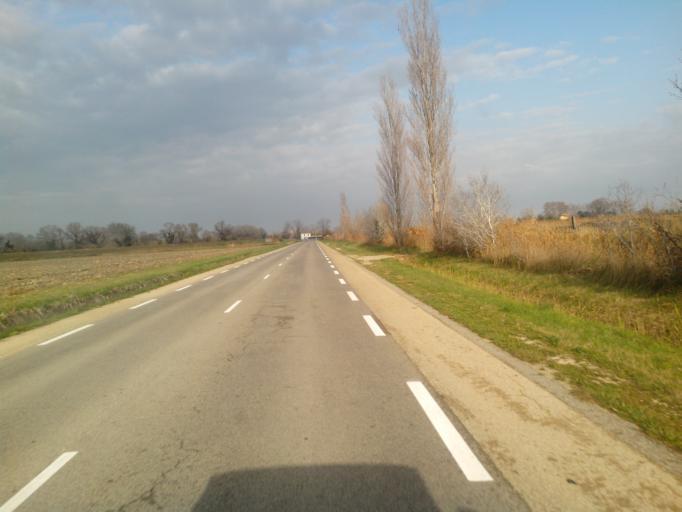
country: FR
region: Languedoc-Roussillon
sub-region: Departement du Gard
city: Saint-Gilles
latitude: 43.5988
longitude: 4.4726
